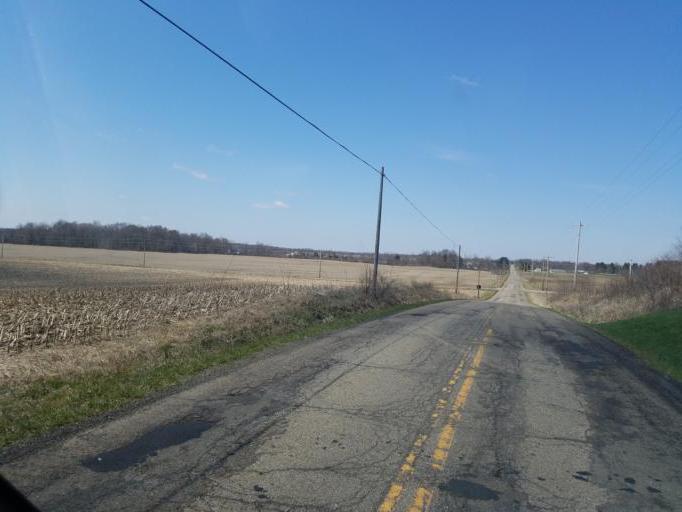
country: US
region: Ohio
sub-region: Knox County
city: Centerburg
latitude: 40.3170
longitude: -82.6467
